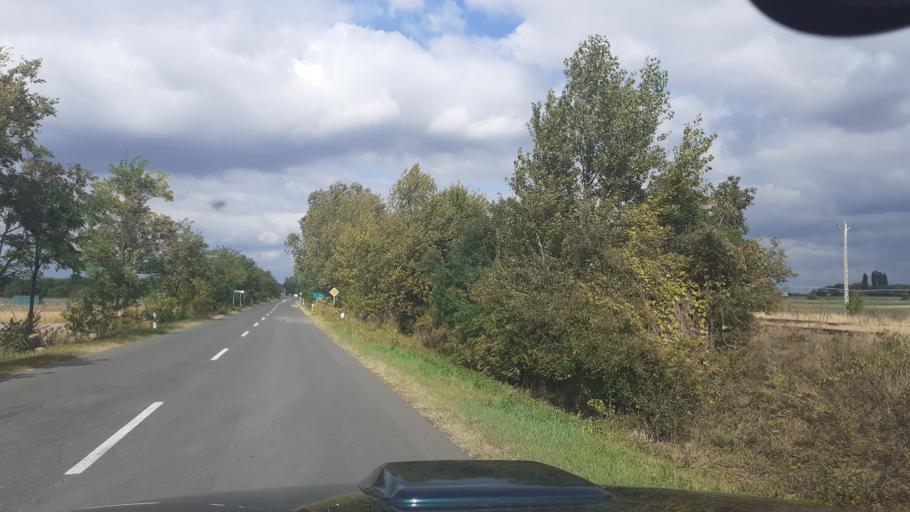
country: HU
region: Bacs-Kiskun
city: Apostag
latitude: 46.8812
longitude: 18.9776
